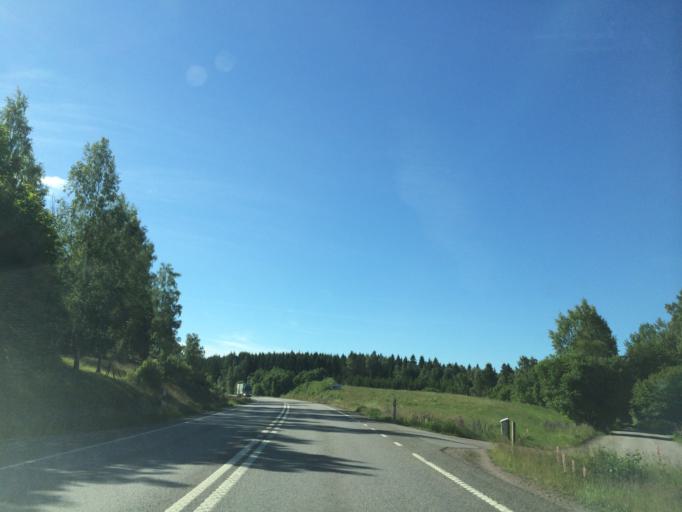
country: SE
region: OEstergoetland
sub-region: Motala Kommun
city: Motala
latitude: 58.6355
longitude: 14.9594
